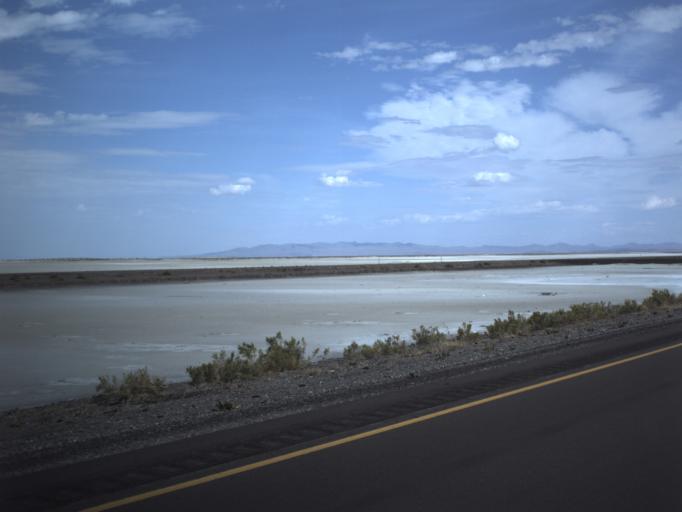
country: US
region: Utah
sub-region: Tooele County
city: Wendover
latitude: 40.7297
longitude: -113.4500
